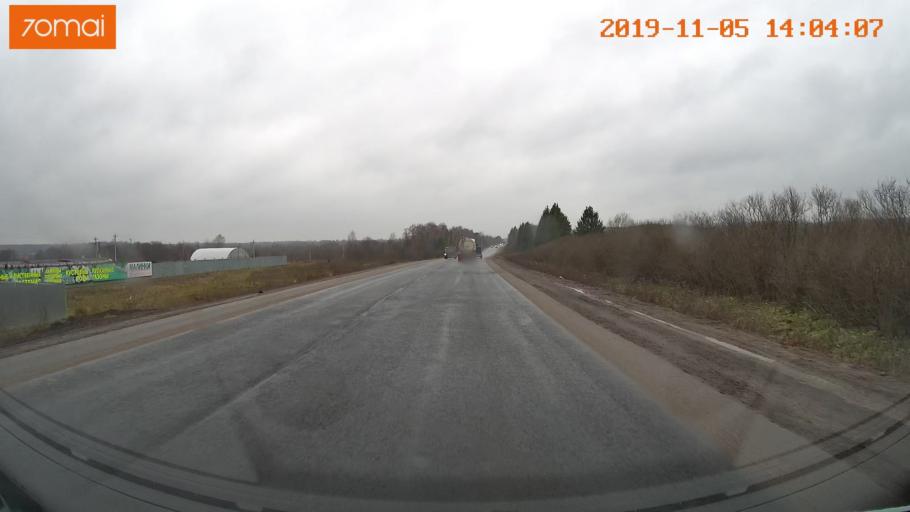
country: RU
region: Ivanovo
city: Kokhma
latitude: 56.9973
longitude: 41.1823
